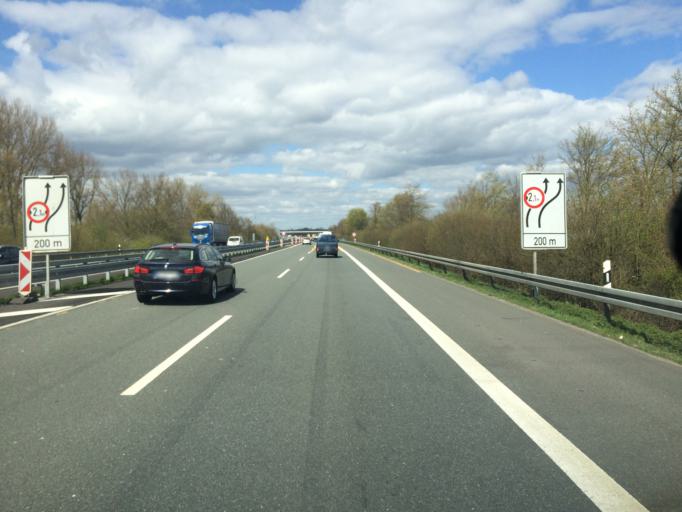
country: DE
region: North Rhine-Westphalia
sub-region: Regierungsbezirk Munster
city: Gescher
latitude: 51.9425
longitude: 7.0448
